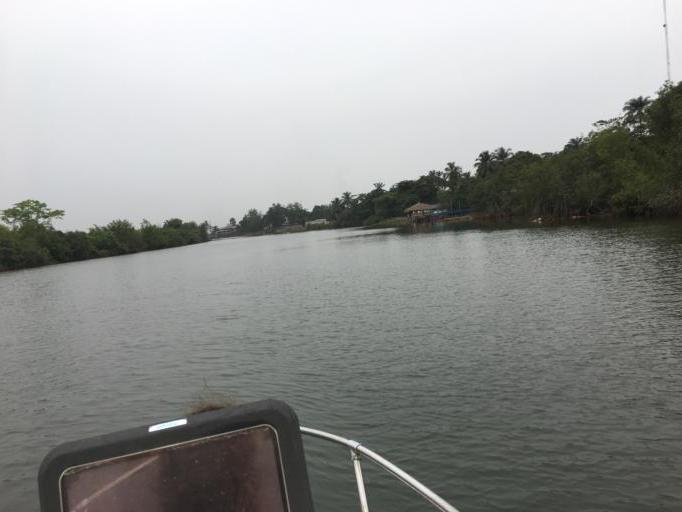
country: LR
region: Montserrado
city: Monrovia
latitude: 6.3809
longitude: -10.7807
